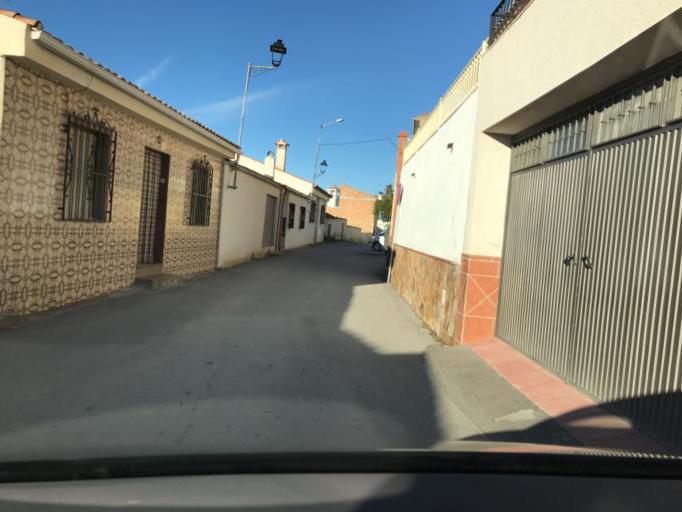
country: ES
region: Andalusia
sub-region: Provincia de Granada
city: Calicasas
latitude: 37.2731
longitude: -3.6167
